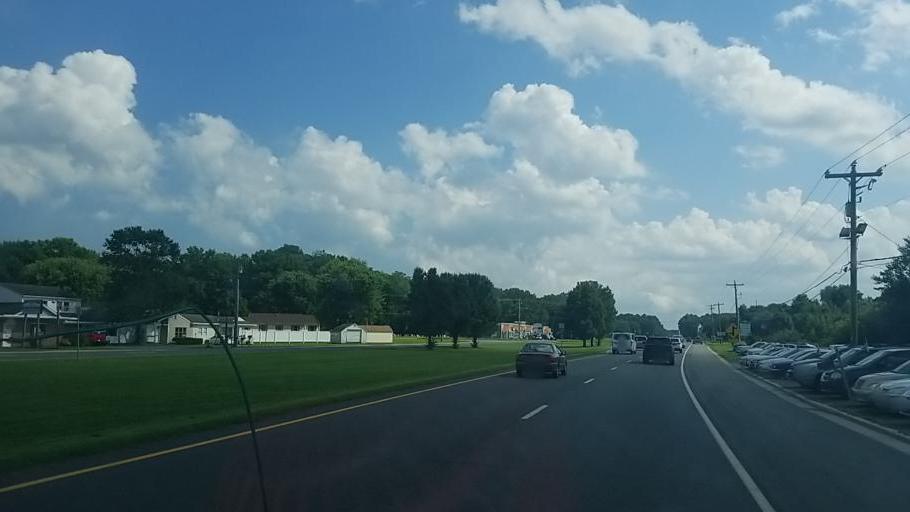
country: US
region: Delaware
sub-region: Sussex County
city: Selbyville
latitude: 38.5143
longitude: -75.2388
